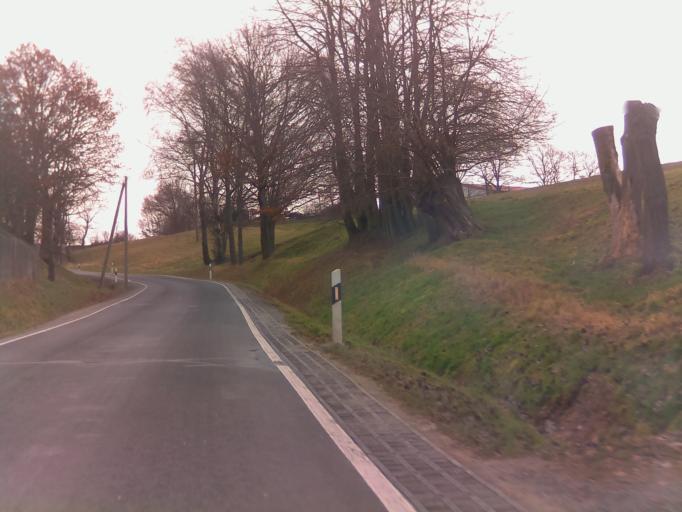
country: DE
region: Thuringia
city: Bocka
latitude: 50.8199
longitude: 11.9763
